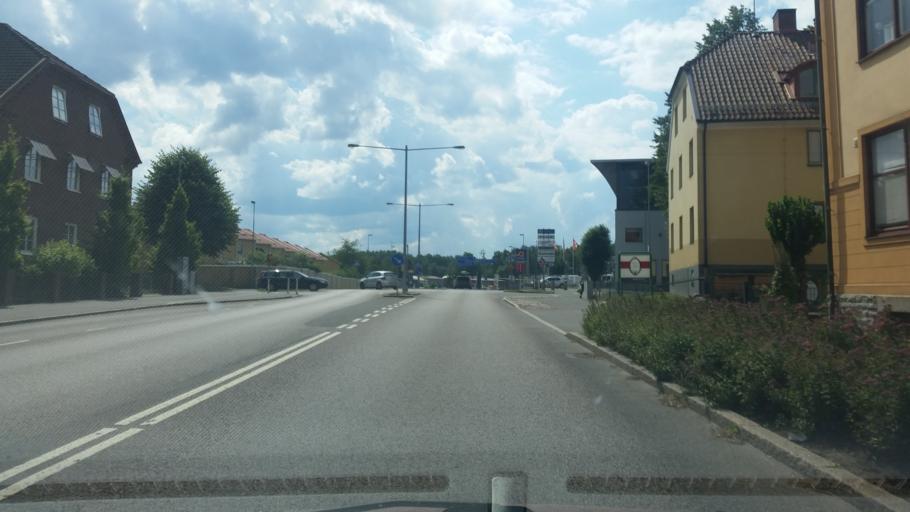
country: SE
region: Vaestra Goetaland
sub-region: Skovde Kommun
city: Skoevde
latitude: 58.3867
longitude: 13.8378
